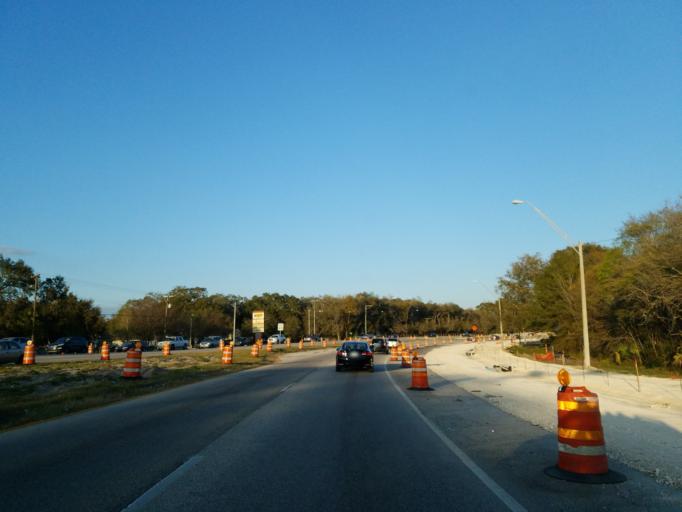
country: US
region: Florida
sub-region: Hillsborough County
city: University
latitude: 28.0798
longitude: -82.4250
